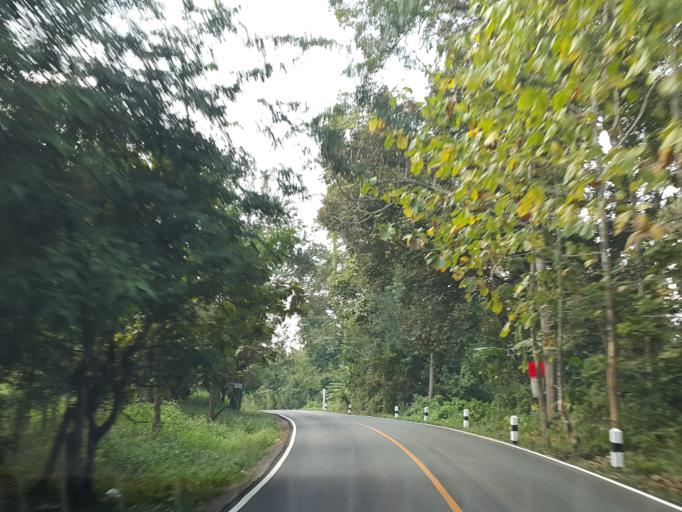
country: TH
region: Chiang Mai
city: Mae On
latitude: 18.8997
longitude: 99.2586
